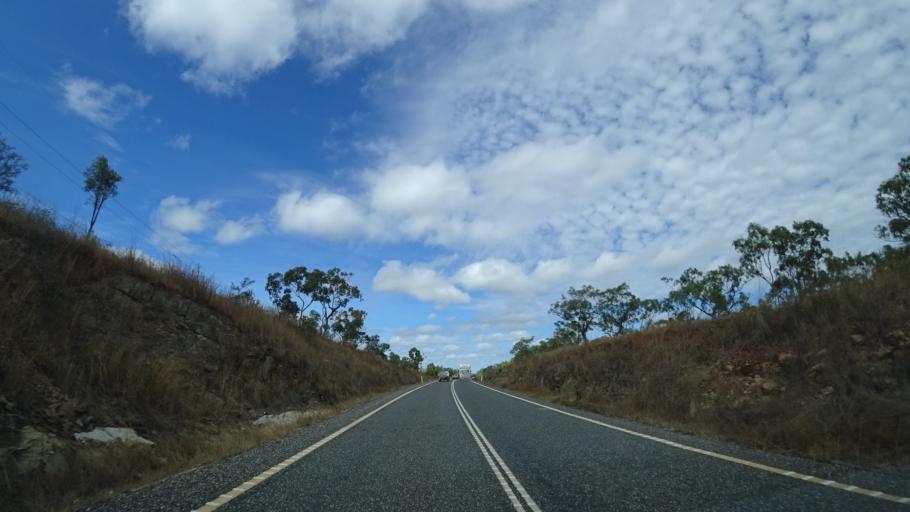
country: AU
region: Queensland
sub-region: Cairns
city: Port Douglas
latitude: -16.3409
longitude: 144.7259
